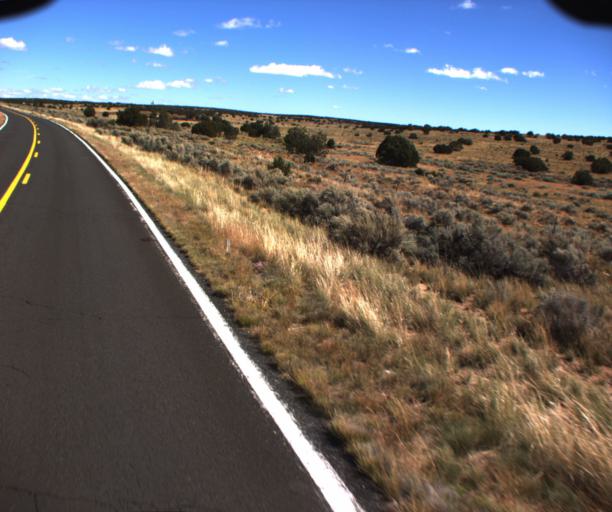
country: US
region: Arizona
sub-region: Apache County
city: Houck
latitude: 34.9348
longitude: -109.1880
